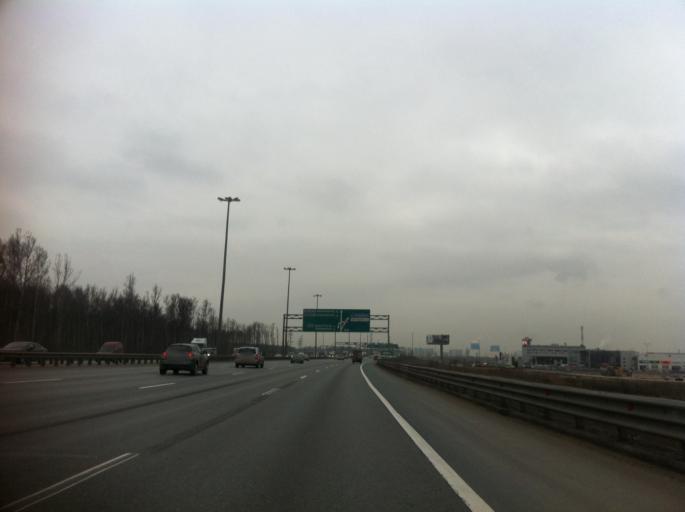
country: RU
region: Leningrad
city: Rybatskoye
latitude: 59.9014
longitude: 30.5260
